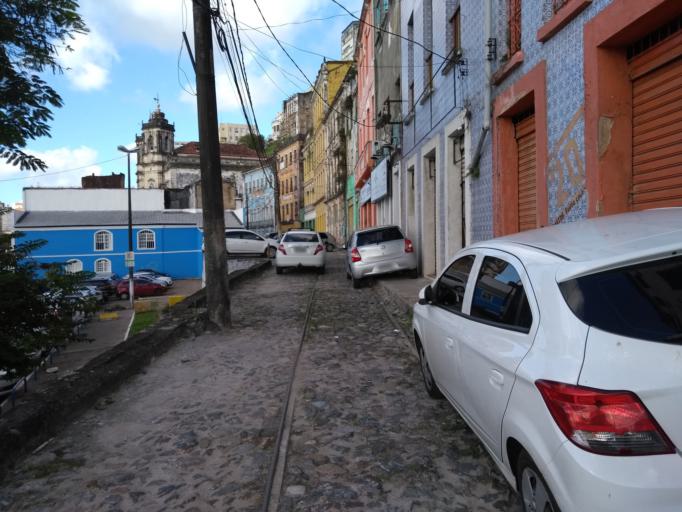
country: BR
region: Bahia
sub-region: Salvador
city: Salvador
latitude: -12.9762
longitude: -38.5153
